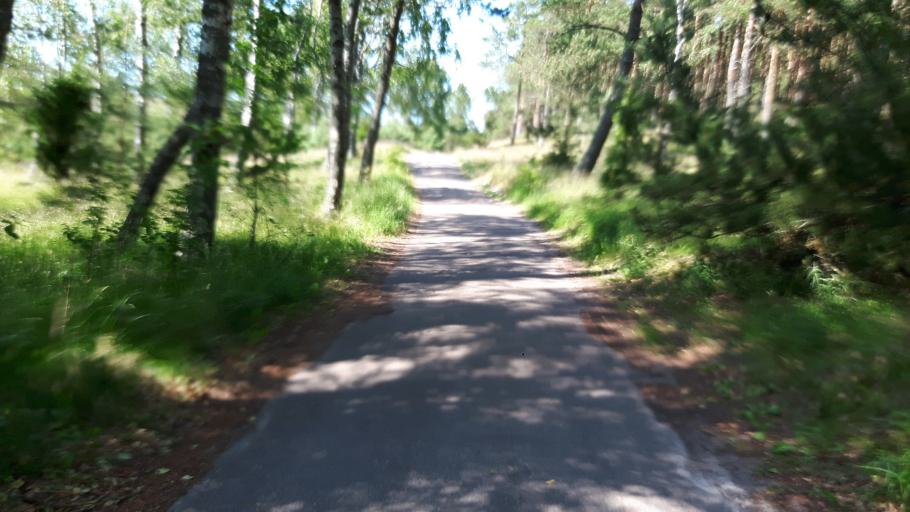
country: LT
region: Klaipedos apskritis
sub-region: Klaipeda
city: Klaipeda
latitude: 55.6828
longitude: 21.1045
